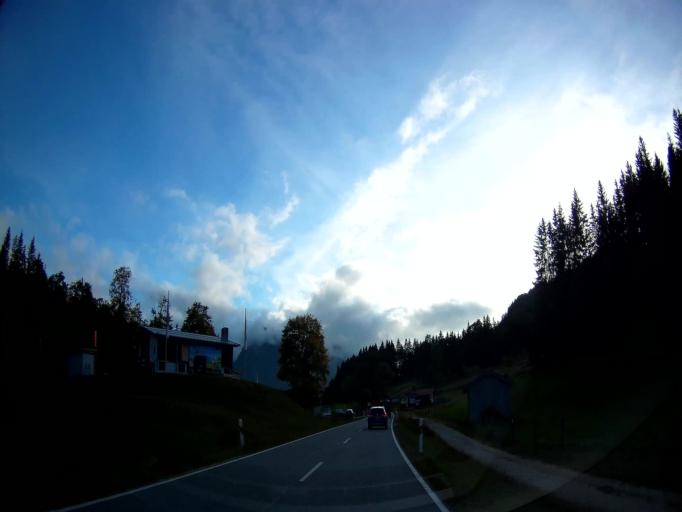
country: DE
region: Bavaria
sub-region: Upper Bavaria
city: Ramsau
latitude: 47.6279
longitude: 12.9060
